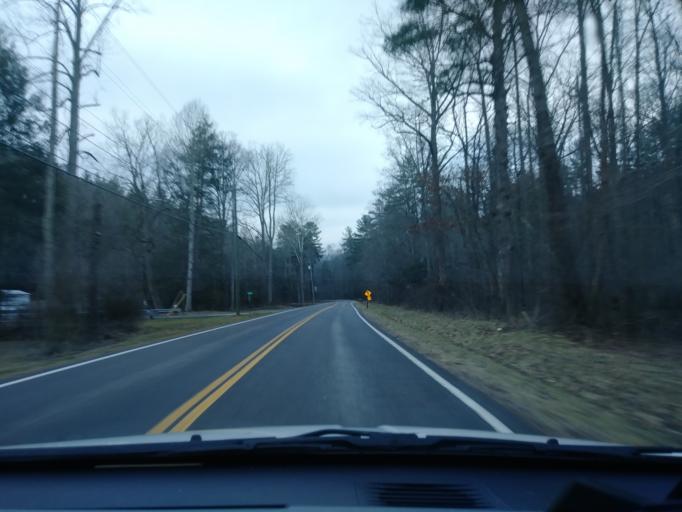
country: US
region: Tennessee
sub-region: Unicoi County
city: Unicoi
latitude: 36.1772
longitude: -82.2802
